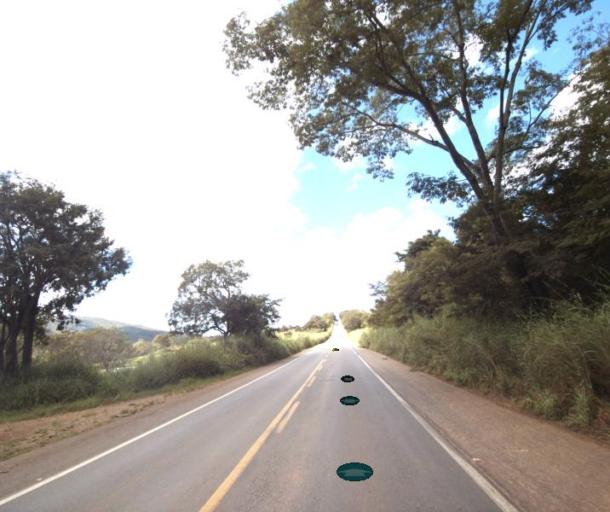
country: BR
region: Goias
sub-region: Petrolina De Goias
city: Petrolina de Goias
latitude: -15.9752
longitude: -49.1664
